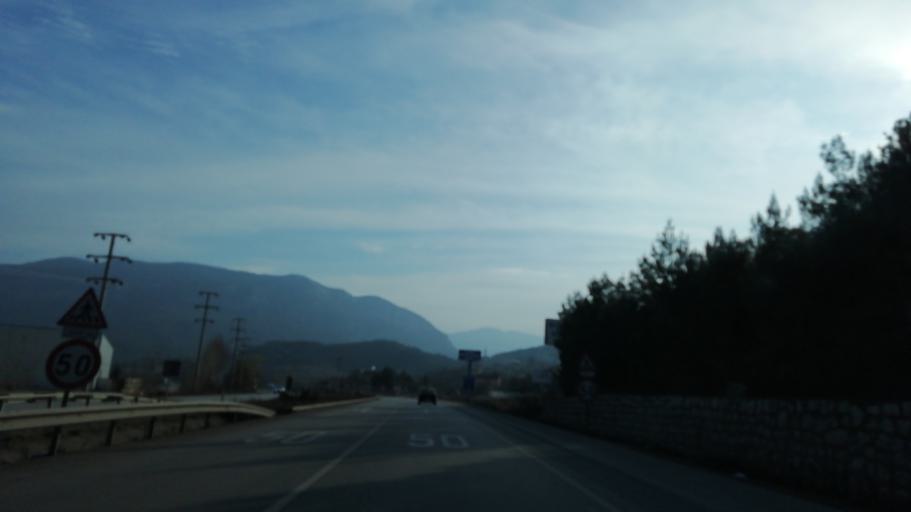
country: TR
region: Karabuk
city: Karabuk
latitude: 41.1371
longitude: 32.6671
